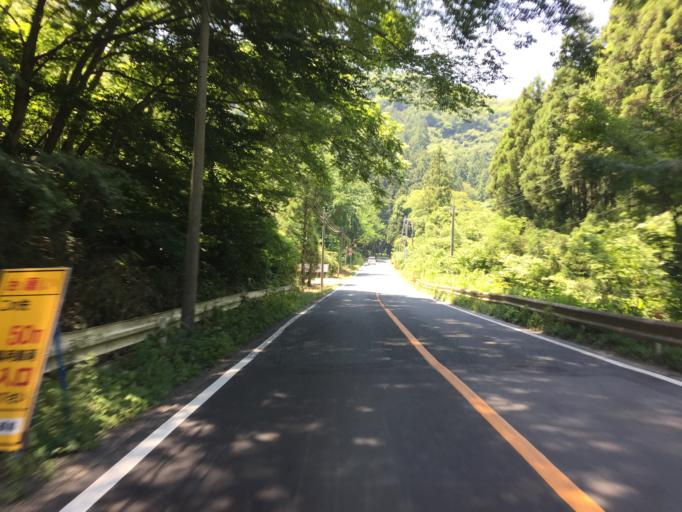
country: JP
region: Miyagi
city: Marumori
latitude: 37.7795
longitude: 140.8072
